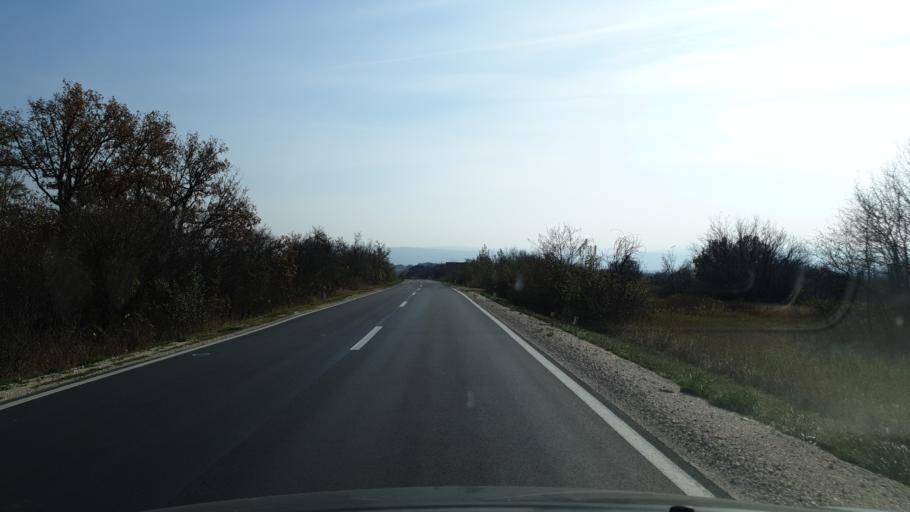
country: RS
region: Central Serbia
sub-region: Borski Okrug
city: Bor
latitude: 43.9802
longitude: 22.0729
